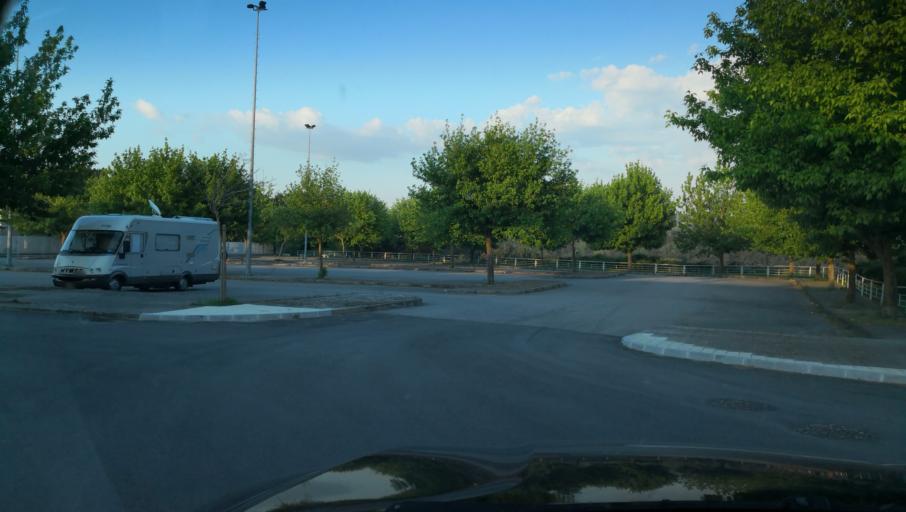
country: PT
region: Vila Real
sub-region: Vila Real
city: Vila Real
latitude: 41.2869
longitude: -7.7551
